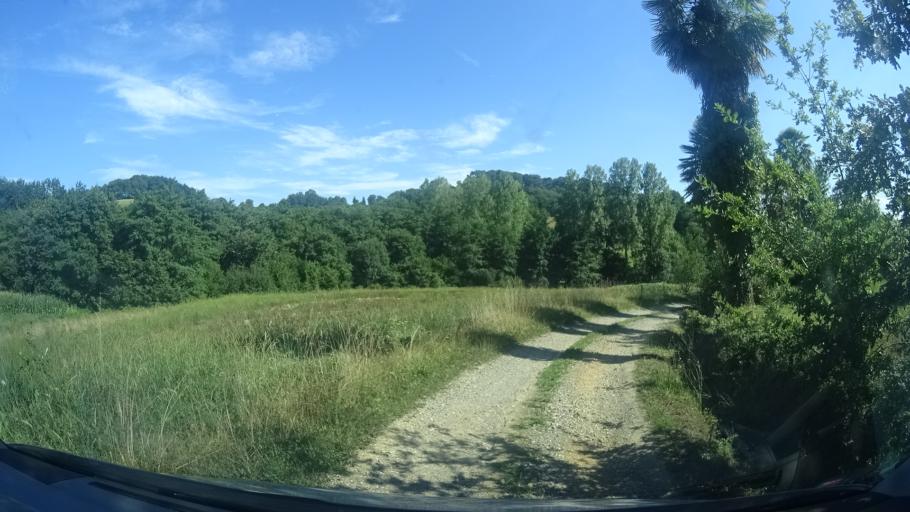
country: FR
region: Aquitaine
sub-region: Departement des Pyrenees-Atlantiques
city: Mont
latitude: 43.4916
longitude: -0.6905
